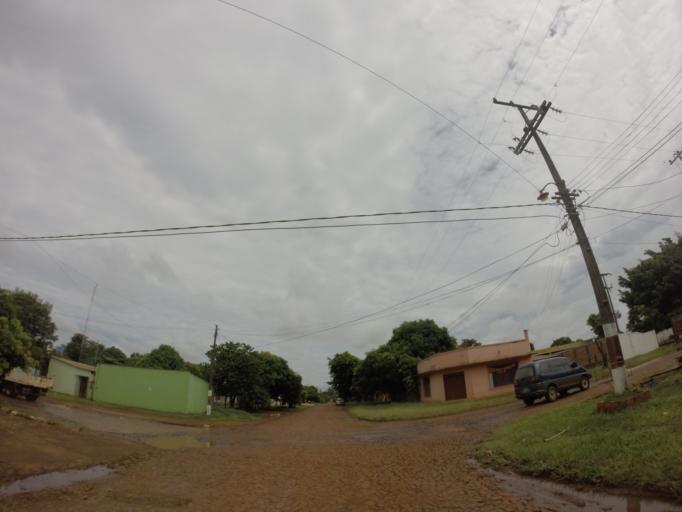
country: PY
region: Alto Parana
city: Ciudad del Este
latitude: -25.3996
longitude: -54.6447
